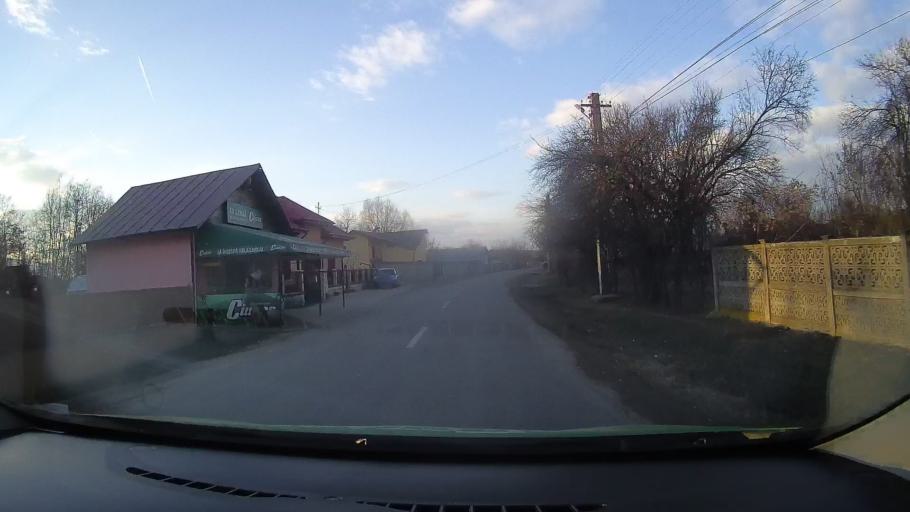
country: RO
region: Dambovita
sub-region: Comuna Gura Ocnitei
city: Adanca
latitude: 44.9112
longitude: 25.6155
